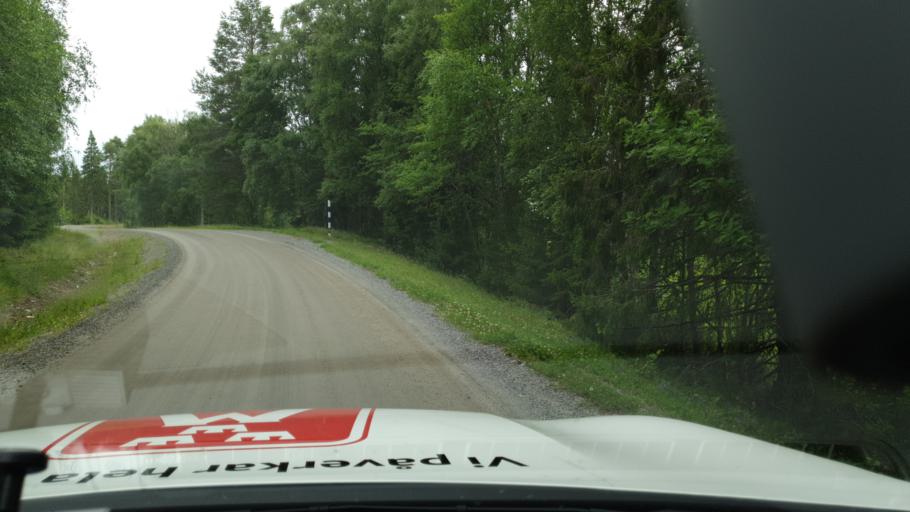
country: SE
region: Vaesterbotten
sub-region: Robertsfors Kommun
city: Robertsfors
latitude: 64.0121
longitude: 20.8992
